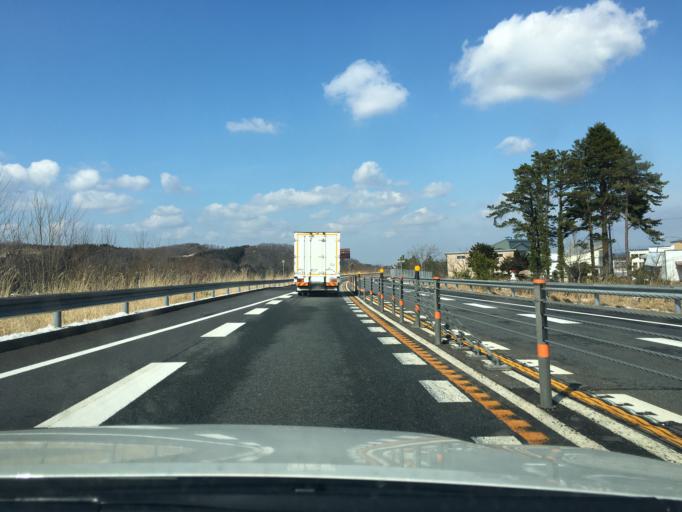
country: JP
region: Yamagata
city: Tsuruoka
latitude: 38.6112
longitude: 139.8421
